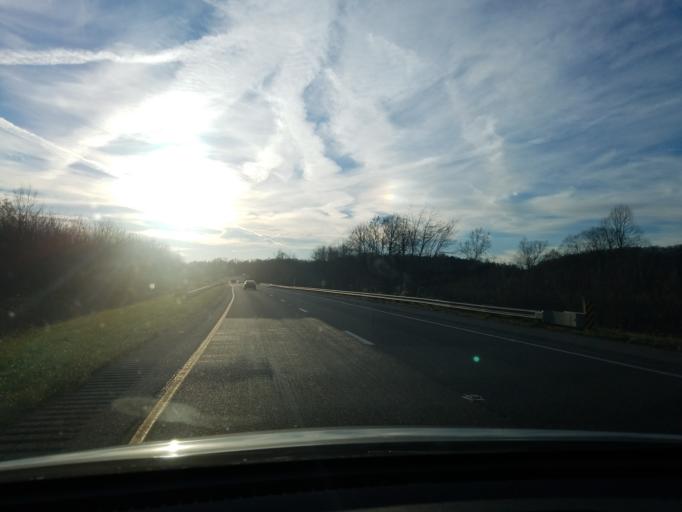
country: US
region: Indiana
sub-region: Dubois County
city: Ferdinand
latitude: 38.2102
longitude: -86.7755
